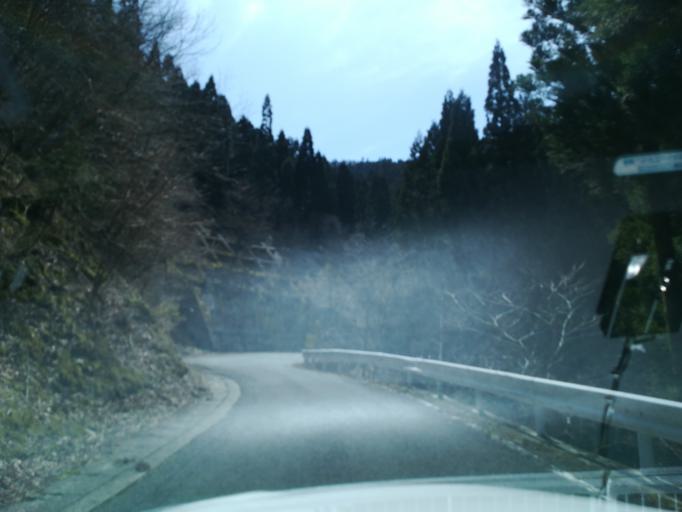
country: JP
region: Tokushima
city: Wakimachi
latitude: 33.8806
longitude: 134.0554
